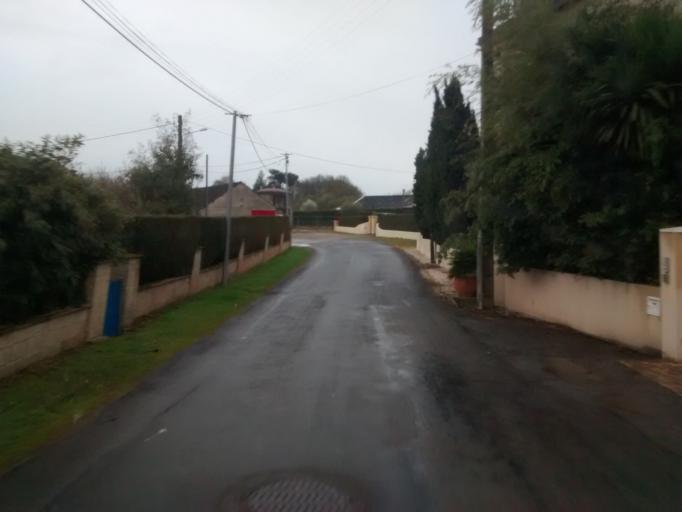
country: FR
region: Brittany
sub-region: Departement du Morbihan
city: Malestroit
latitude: 47.8081
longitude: -2.4022
